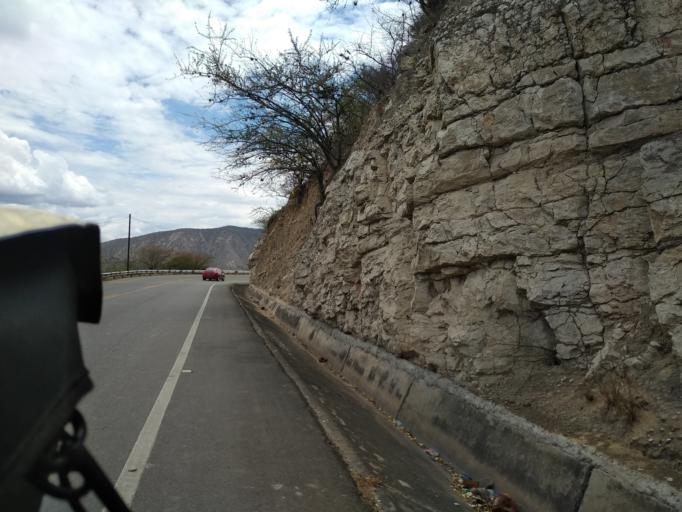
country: PE
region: Cajamarca
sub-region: Provincia de Jaen
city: Bellavista
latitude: -5.7410
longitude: -78.6571
